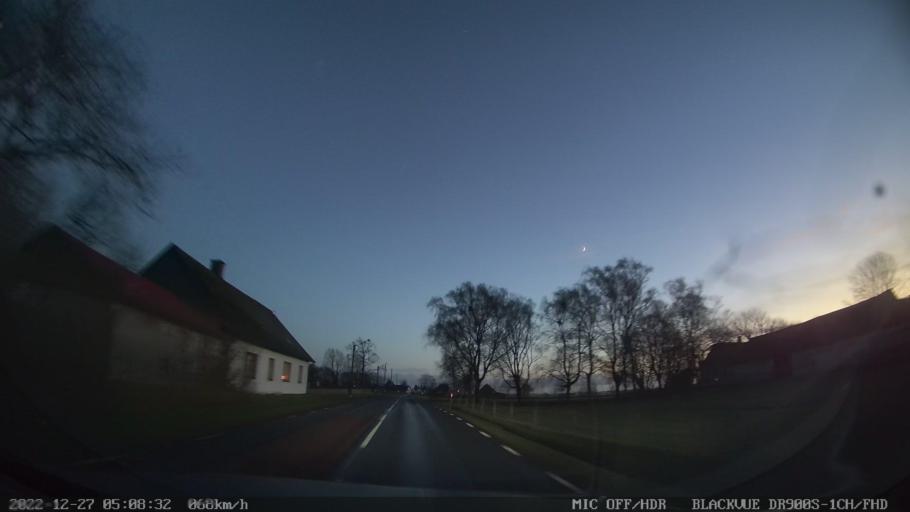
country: SE
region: Skane
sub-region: Simrishamns Kommun
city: Kivik
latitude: 55.5701
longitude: 14.1523
